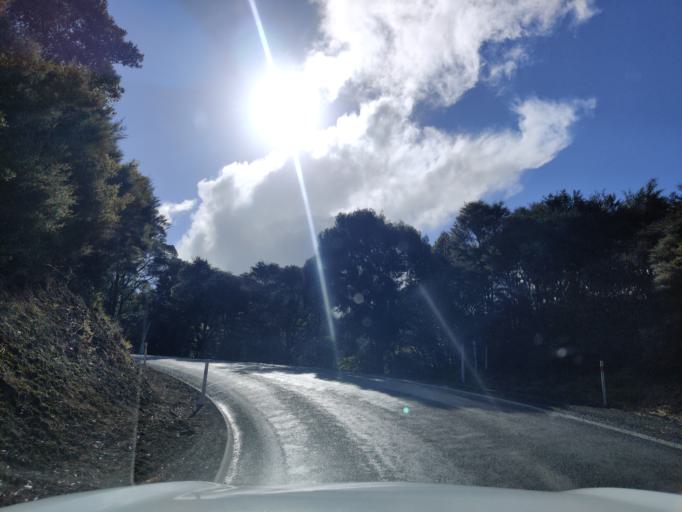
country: NZ
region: Waikato
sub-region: Thames-Coromandel District
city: Whitianga
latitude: -36.7579
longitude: 175.7274
